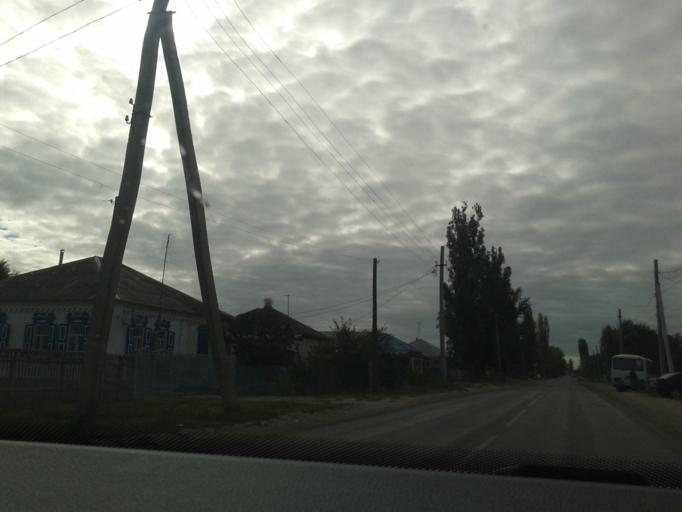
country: RU
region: Volgograd
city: Frolovo
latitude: 49.7705
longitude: 43.6588
